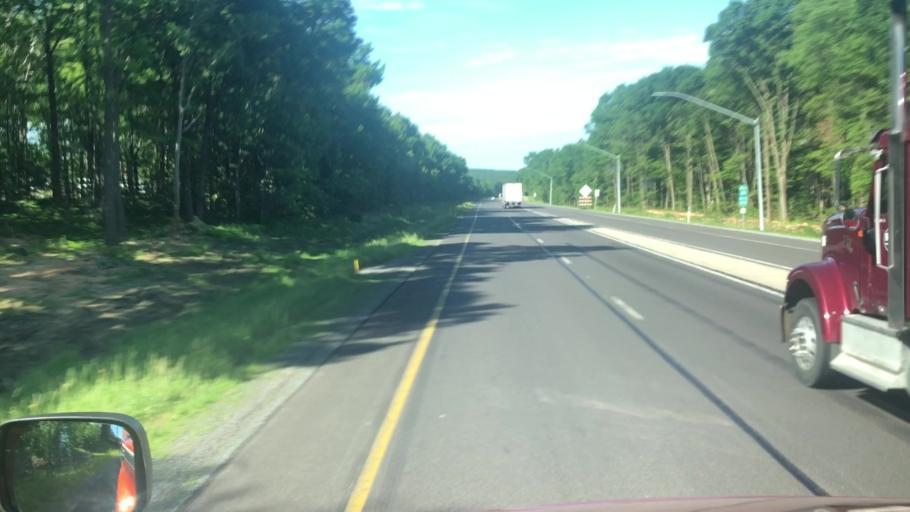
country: US
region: Pennsylvania
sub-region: Centre County
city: Milesburg
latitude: 41.0171
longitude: -77.9548
